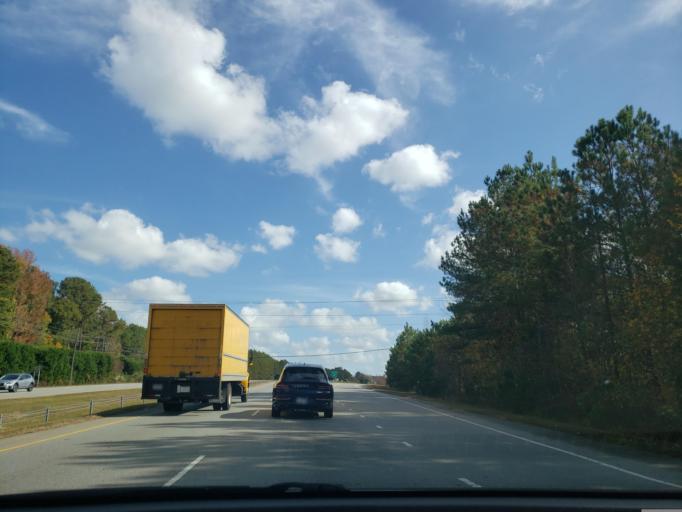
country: US
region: North Carolina
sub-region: Wake County
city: Apex
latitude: 35.7492
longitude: -78.8551
